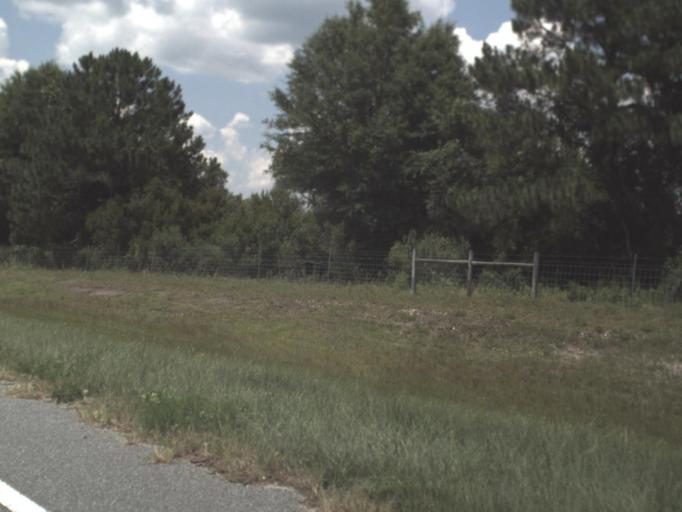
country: US
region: Florida
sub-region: Bradford County
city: Starke
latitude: 30.0195
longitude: -82.0500
